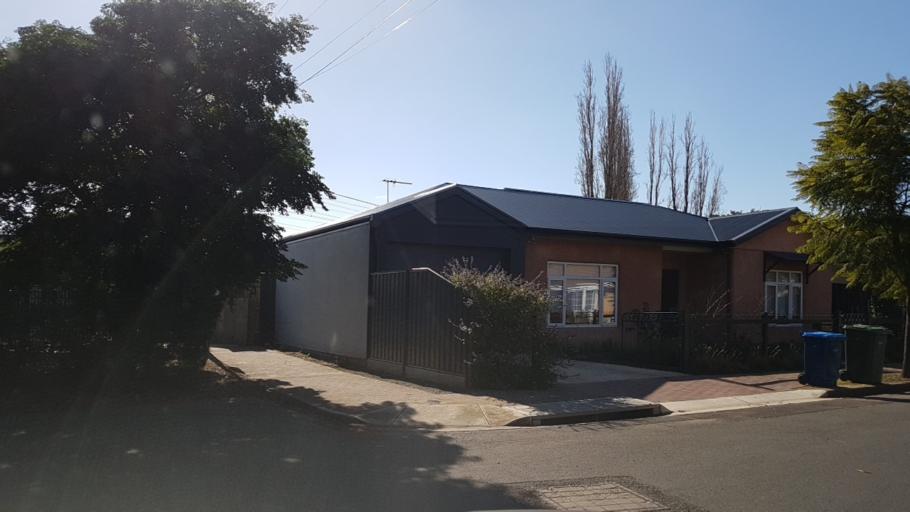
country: AU
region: South Australia
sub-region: Mitcham
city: Clarence Gardens
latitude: -34.9642
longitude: 138.5773
